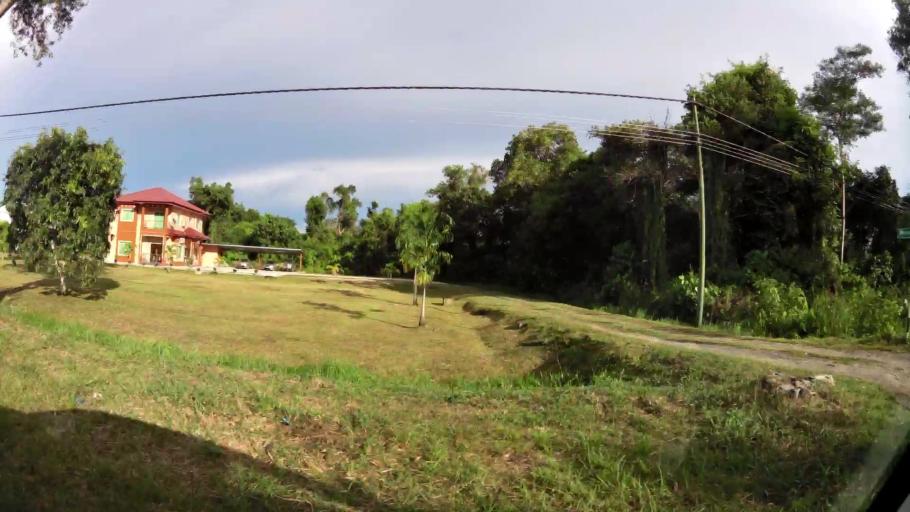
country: BN
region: Brunei and Muara
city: Bandar Seri Begawan
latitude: 4.9591
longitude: 115.0227
